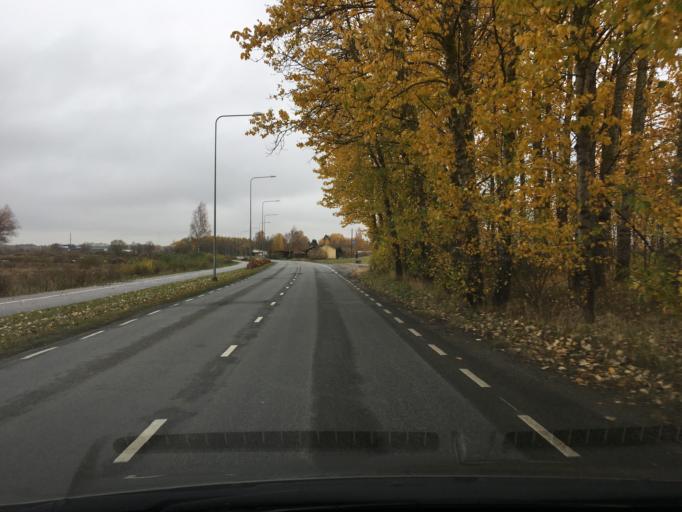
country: EE
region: Tartu
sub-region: Tartu linn
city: Tartu
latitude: 58.3605
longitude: 26.7597
